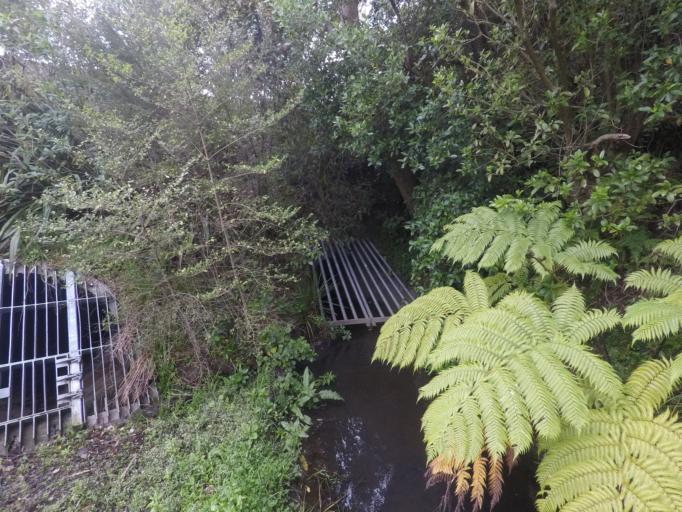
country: NZ
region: Auckland
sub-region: Auckland
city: Tamaki
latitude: -36.9055
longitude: 174.8426
